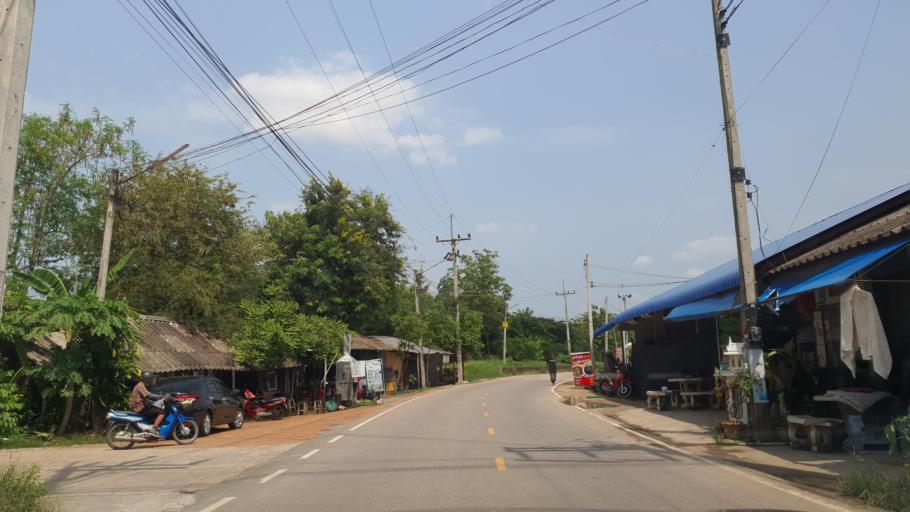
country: TH
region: Lamphun
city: Lamphun
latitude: 18.6019
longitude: 99.0291
